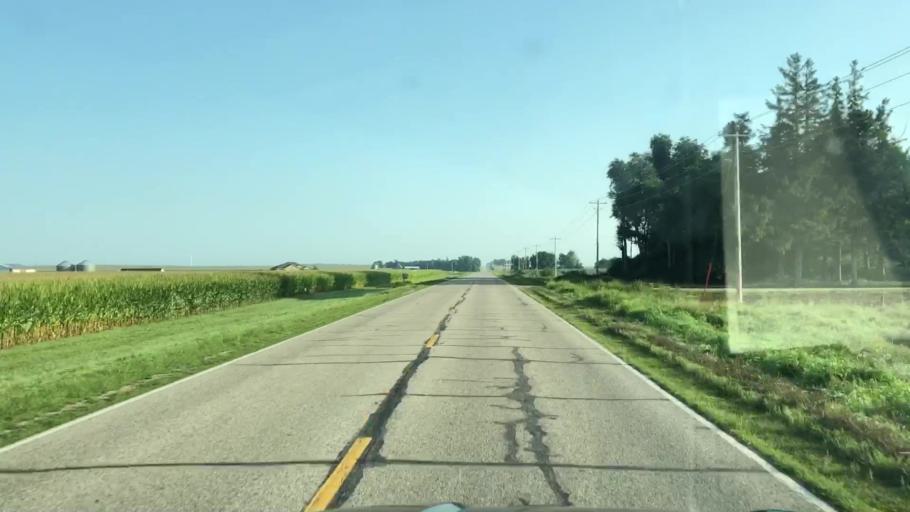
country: US
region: Iowa
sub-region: Lyon County
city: George
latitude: 43.3546
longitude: -95.9984
